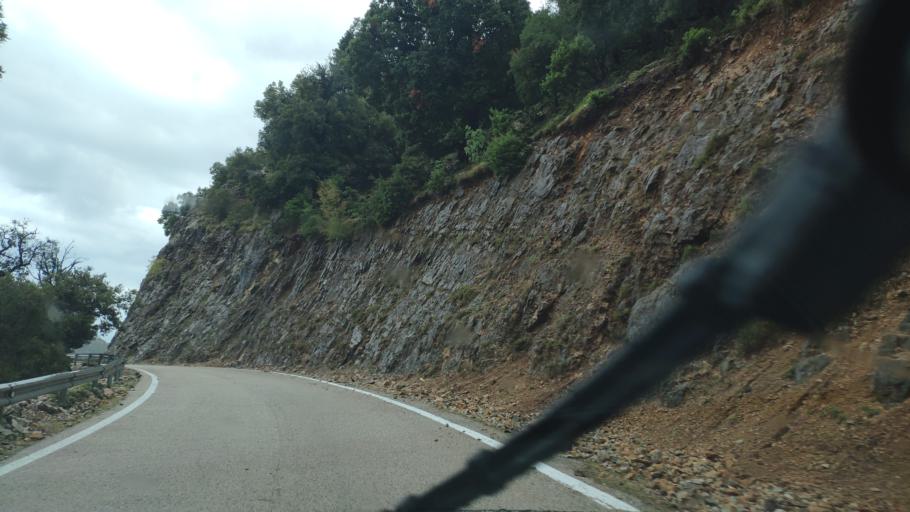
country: GR
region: West Greece
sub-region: Nomos Aitolias kai Akarnanias
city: Krikellos
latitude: 39.0327
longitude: 21.3661
